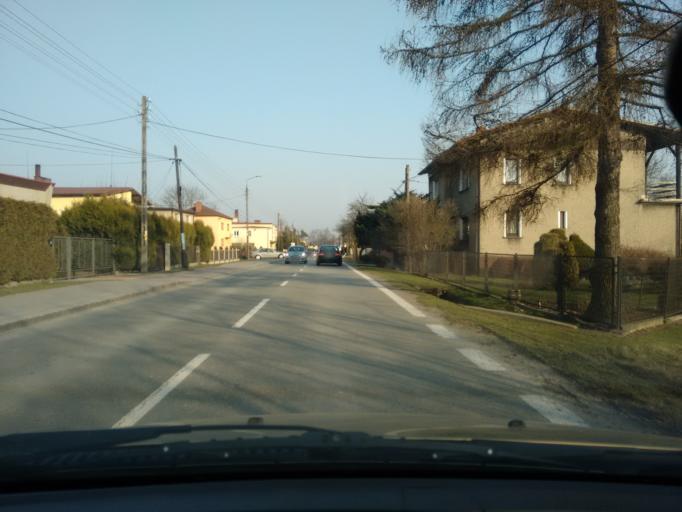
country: PL
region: Silesian Voivodeship
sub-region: Powiat cieszynski
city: Zbytkow
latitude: 49.9154
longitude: 18.7449
